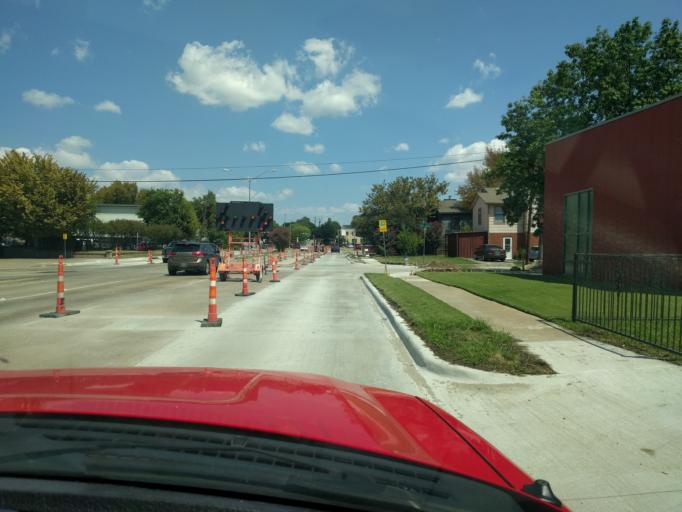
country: US
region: Texas
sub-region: Dallas County
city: Highland Park
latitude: 32.7998
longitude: -96.7578
